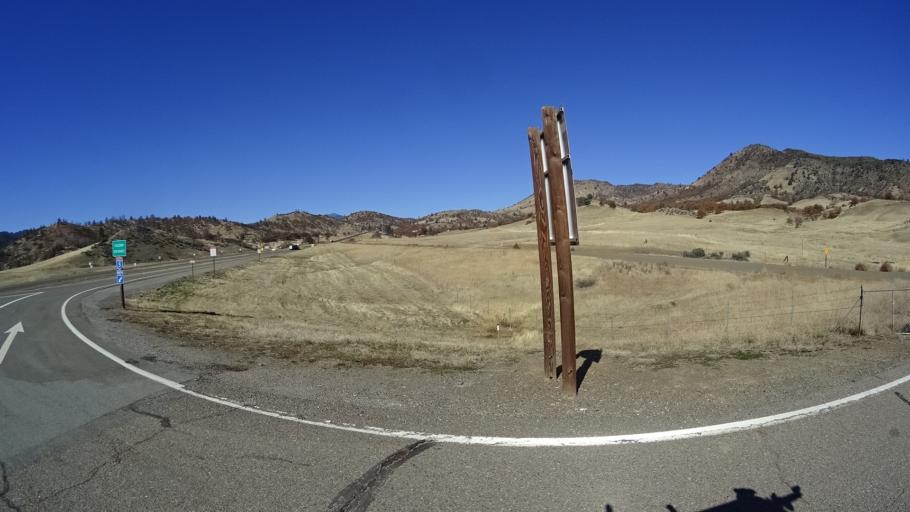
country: US
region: California
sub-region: Siskiyou County
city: Yreka
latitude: 41.9551
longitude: -122.5910
